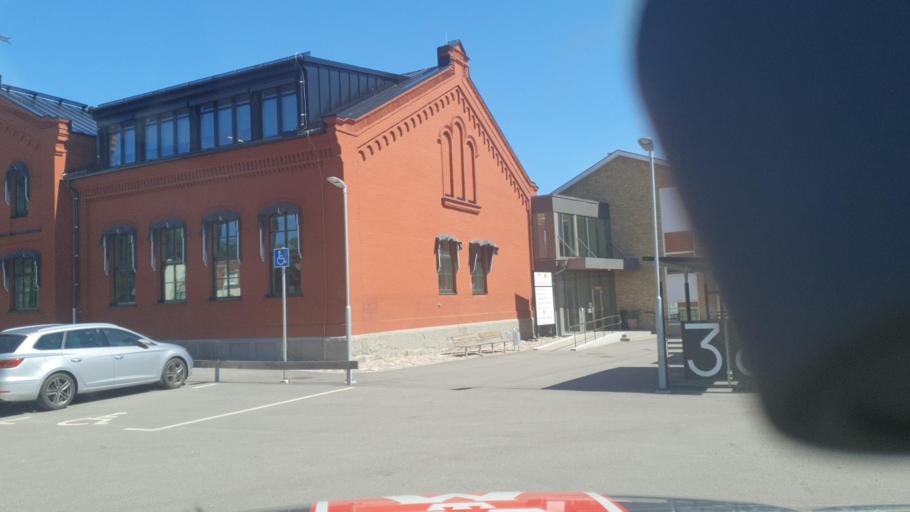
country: SE
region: Kalmar
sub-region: Torsas Kommun
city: Torsas
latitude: 56.4137
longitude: 15.9967
